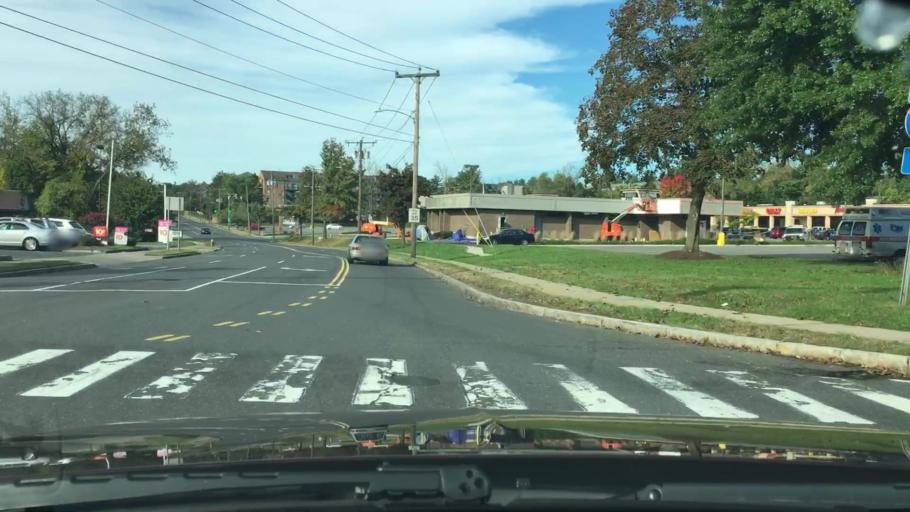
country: US
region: Connecticut
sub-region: Hartford County
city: West Hartford
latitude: 41.7519
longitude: -72.7151
